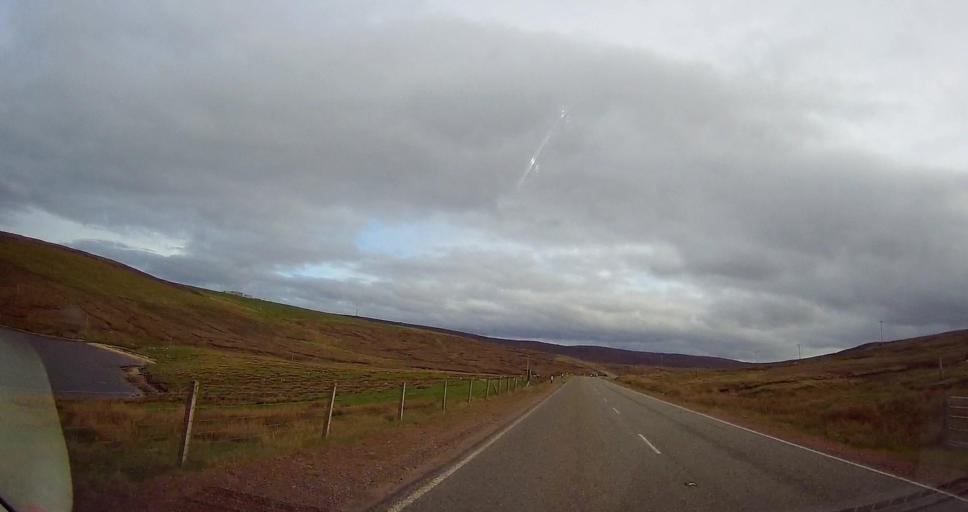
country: GB
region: Scotland
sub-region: Shetland Islands
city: Lerwick
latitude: 60.4602
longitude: -1.2095
